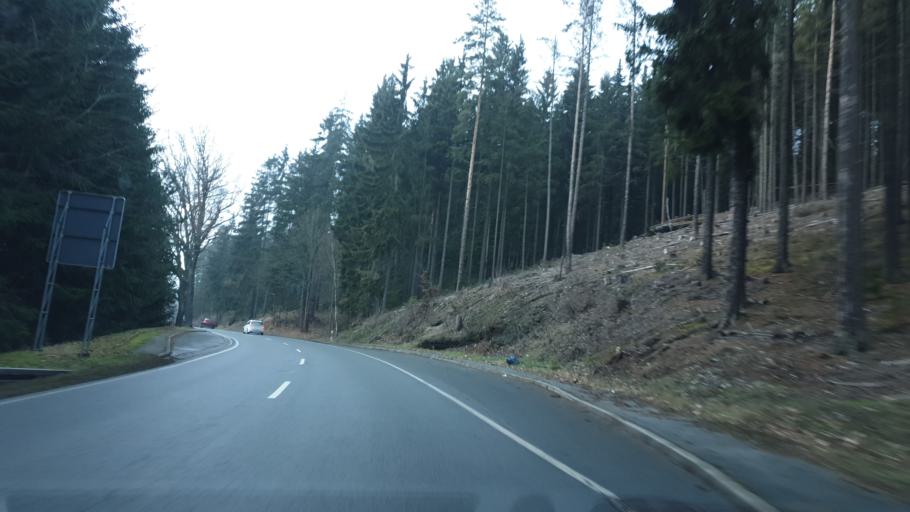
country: DE
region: Saxony
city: Markneukirchen
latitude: 50.2771
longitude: 12.2916
